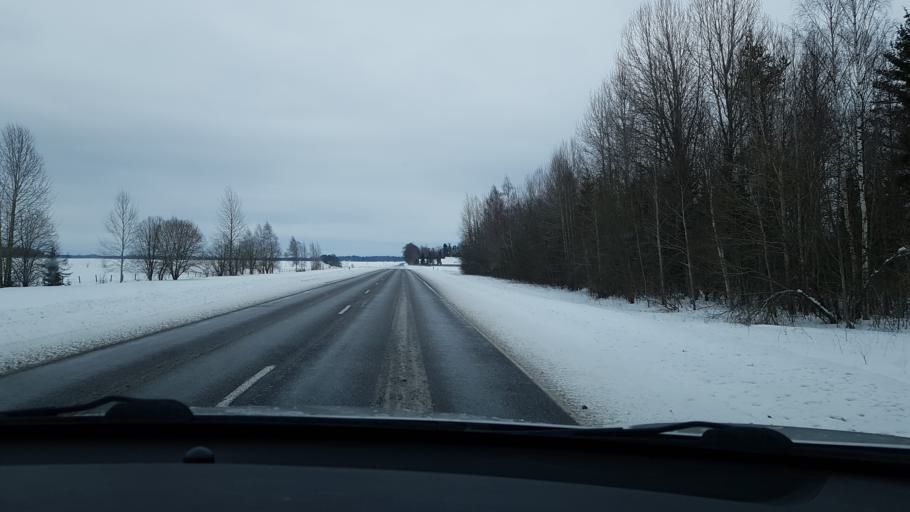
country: EE
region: Jaervamaa
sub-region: Jaerva-Jaani vald
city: Jarva-Jaani
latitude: 59.1265
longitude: 25.7832
